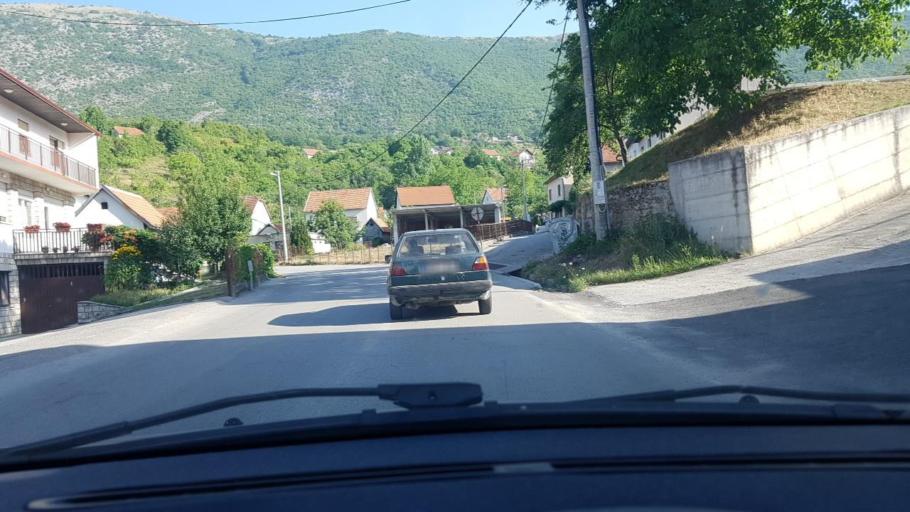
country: BA
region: Federation of Bosnia and Herzegovina
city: Rumboci
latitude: 43.8286
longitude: 17.5164
